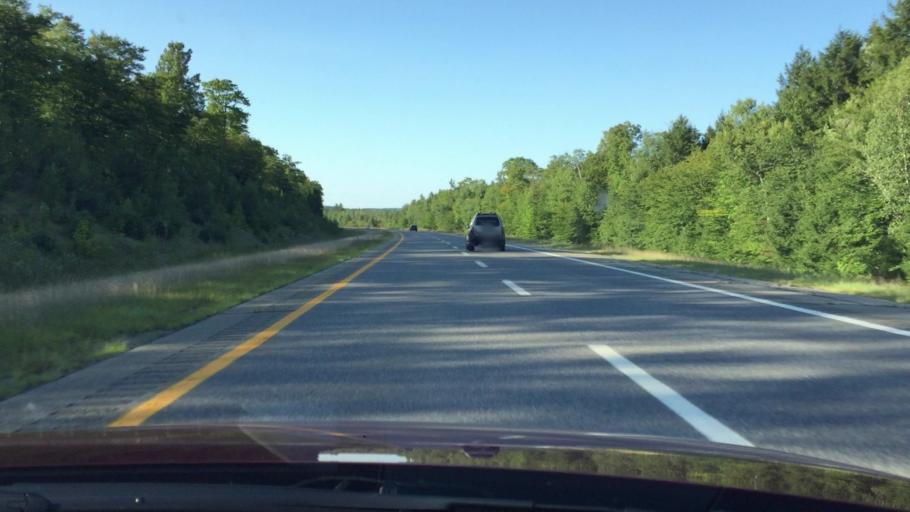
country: US
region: Maine
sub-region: Penobscot County
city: Lincoln
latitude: 45.4270
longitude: -68.5886
